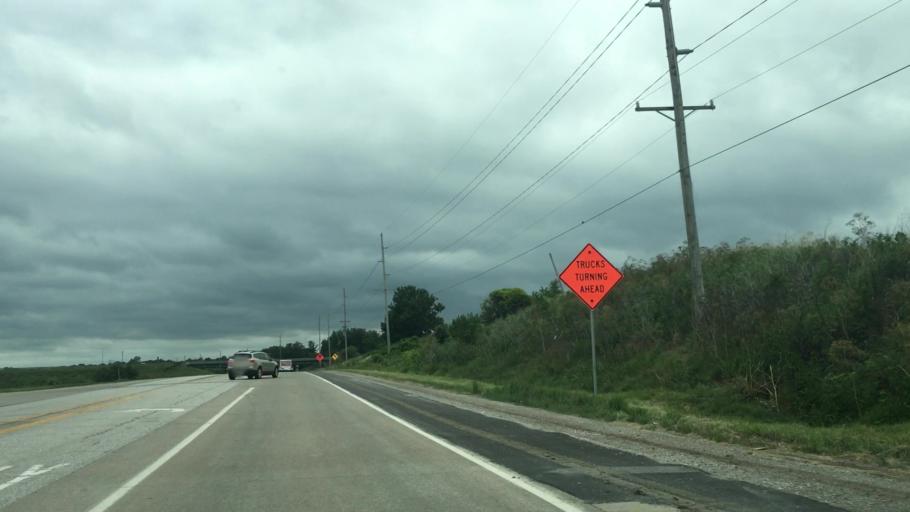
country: US
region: Iowa
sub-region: Johnson County
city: Tiffin
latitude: 41.7041
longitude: -91.6376
